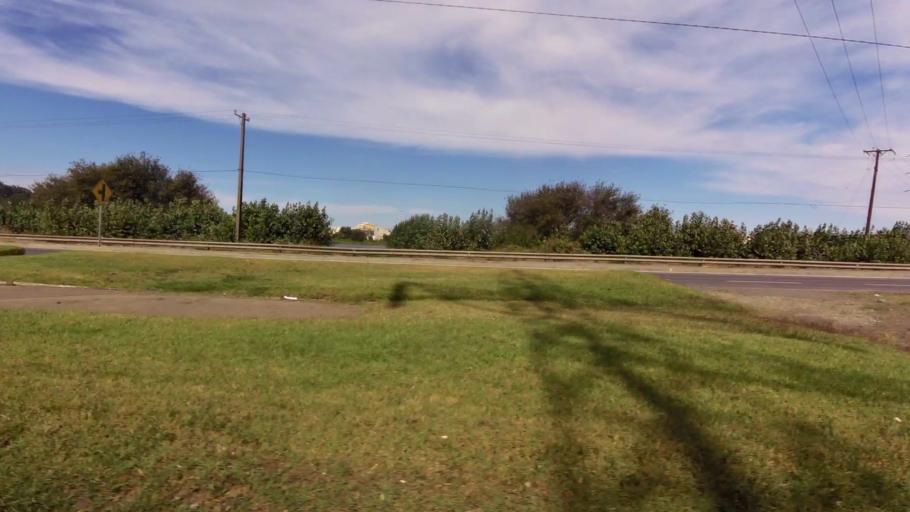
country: CL
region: Biobio
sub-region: Provincia de Concepcion
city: Talcahuano
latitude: -36.7616
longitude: -73.1184
